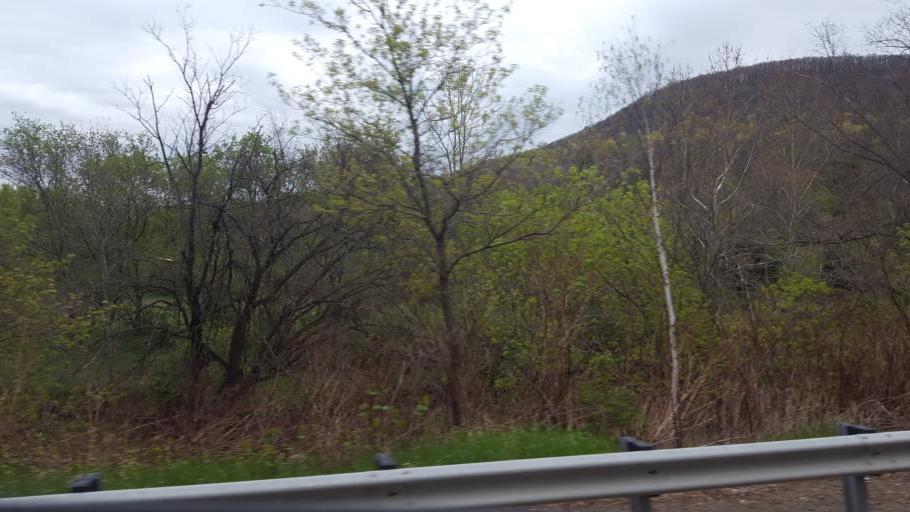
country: US
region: Pennsylvania
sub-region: Tioga County
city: Westfield
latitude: 41.9674
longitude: -77.4507
